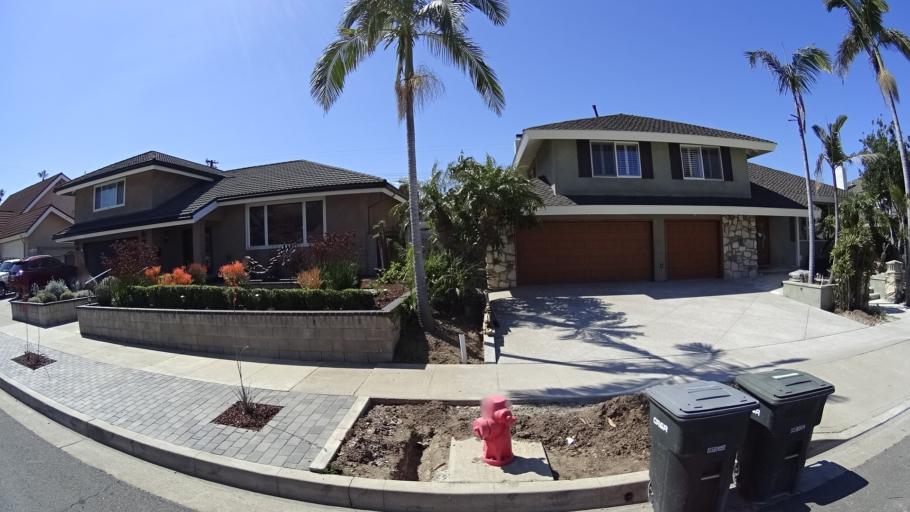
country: US
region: California
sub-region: Orange County
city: Villa Park
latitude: 33.8169
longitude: -117.8237
